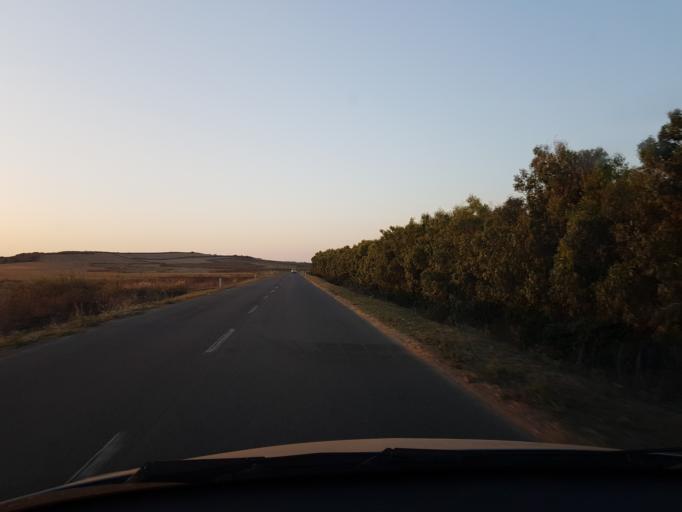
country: IT
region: Sardinia
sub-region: Provincia di Oristano
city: Nurachi
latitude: 39.9717
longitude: 8.4527
